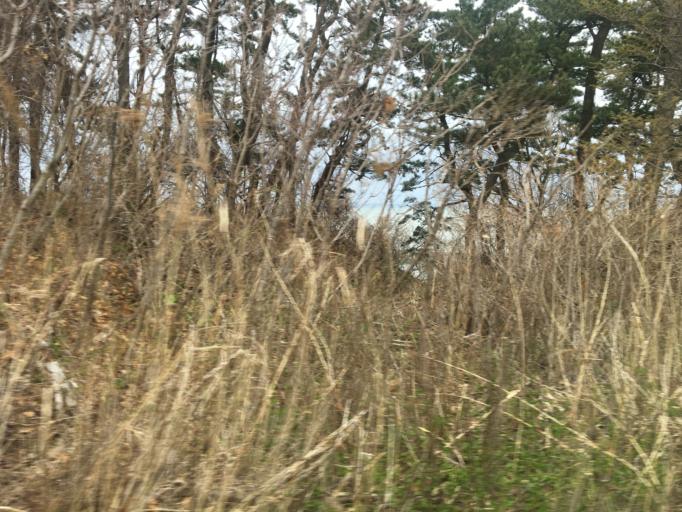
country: JP
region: Aomori
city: Shimokizukuri
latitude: 40.6670
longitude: 139.9422
